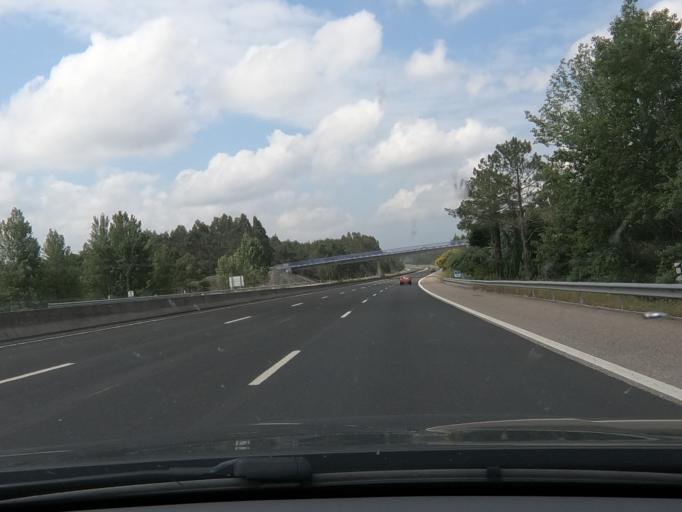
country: PT
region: Leiria
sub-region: Leiria
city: Maceira
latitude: 39.6781
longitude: -8.9408
